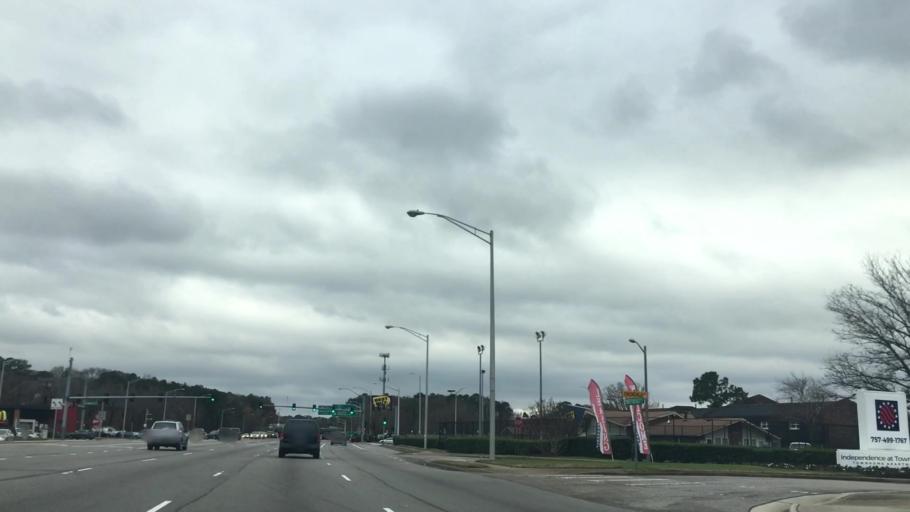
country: US
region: Virginia
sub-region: City of Chesapeake
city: Chesapeake
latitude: 36.8389
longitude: -76.1371
